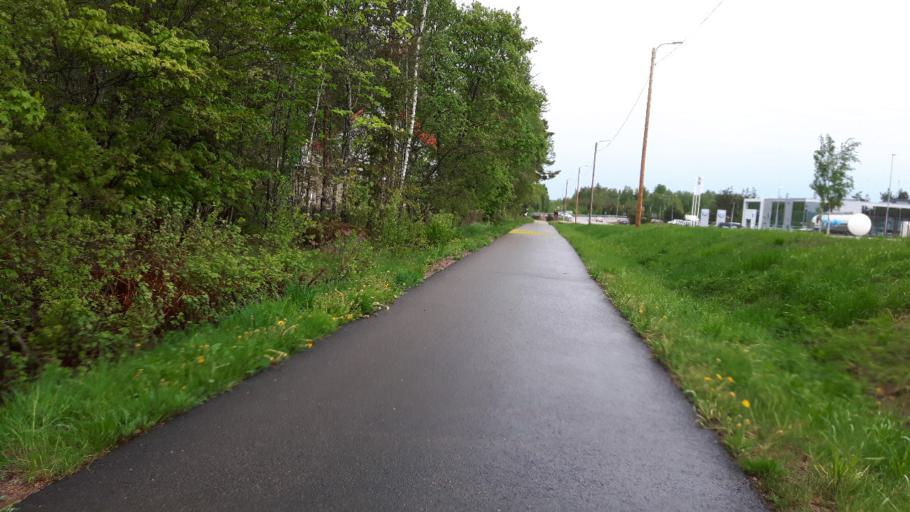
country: FI
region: Kymenlaakso
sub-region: Kotka-Hamina
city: Karhula
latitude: 60.5398
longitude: 26.9705
